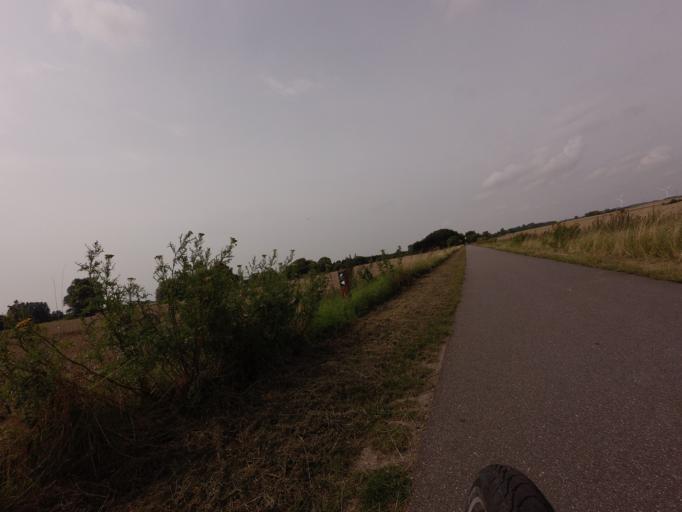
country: DK
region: Zealand
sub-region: Naestved Kommune
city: Naestved
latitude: 55.2564
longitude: 11.6557
